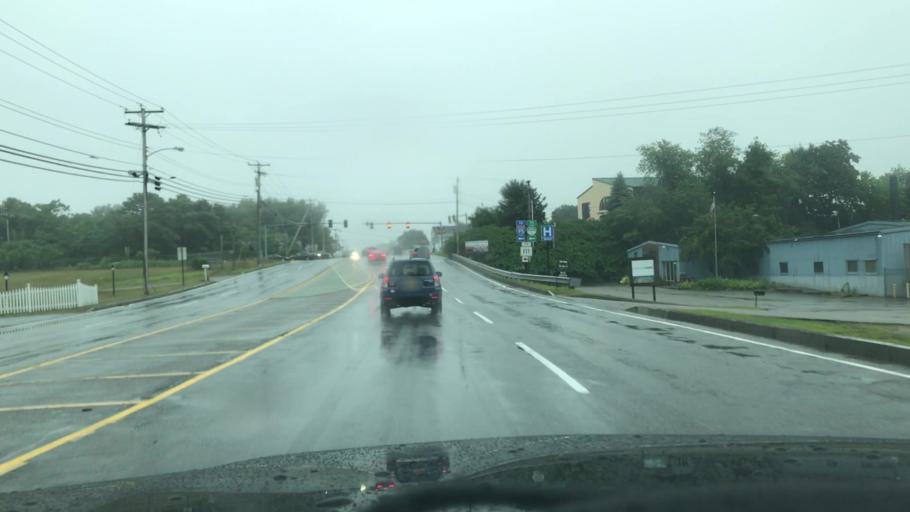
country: US
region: Maine
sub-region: York County
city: Biddeford
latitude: 43.4681
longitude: -70.4859
